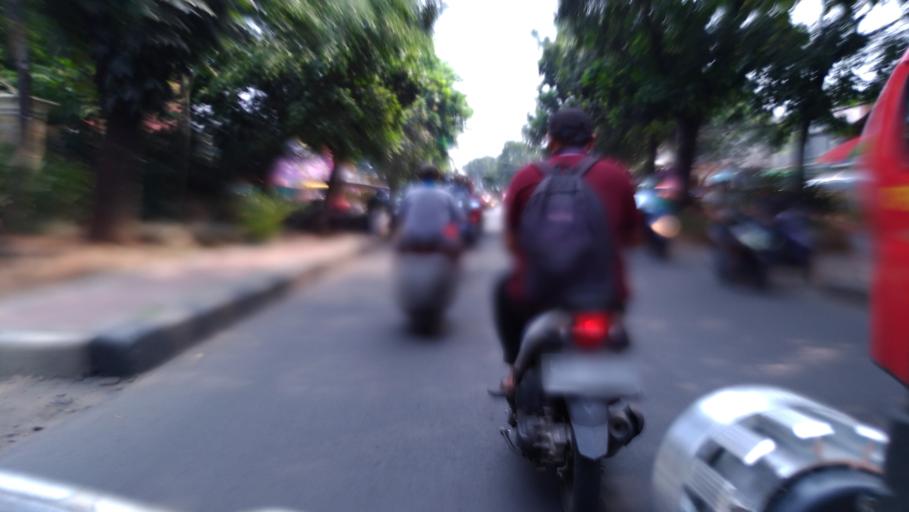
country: ID
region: West Java
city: Depok
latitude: -6.3519
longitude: 106.8847
